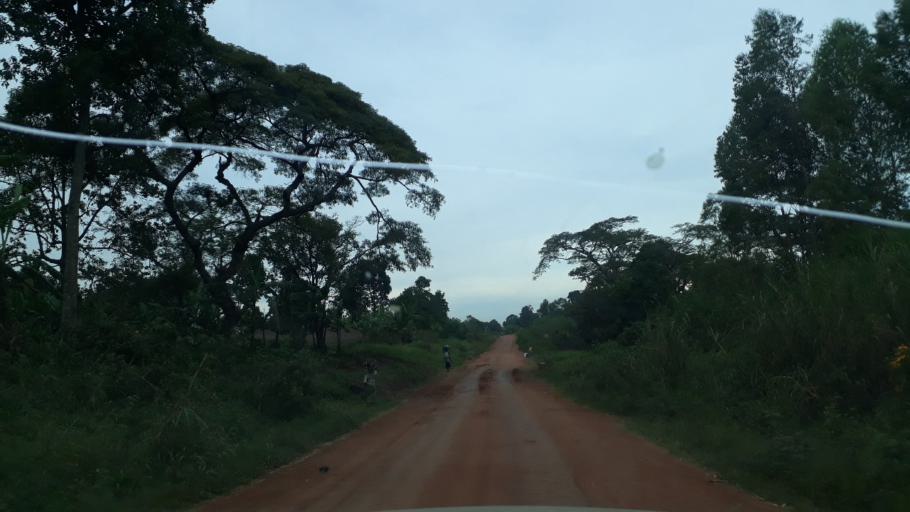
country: UG
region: Northern Region
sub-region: Zombo District
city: Paidha
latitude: 2.1698
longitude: 30.6968
